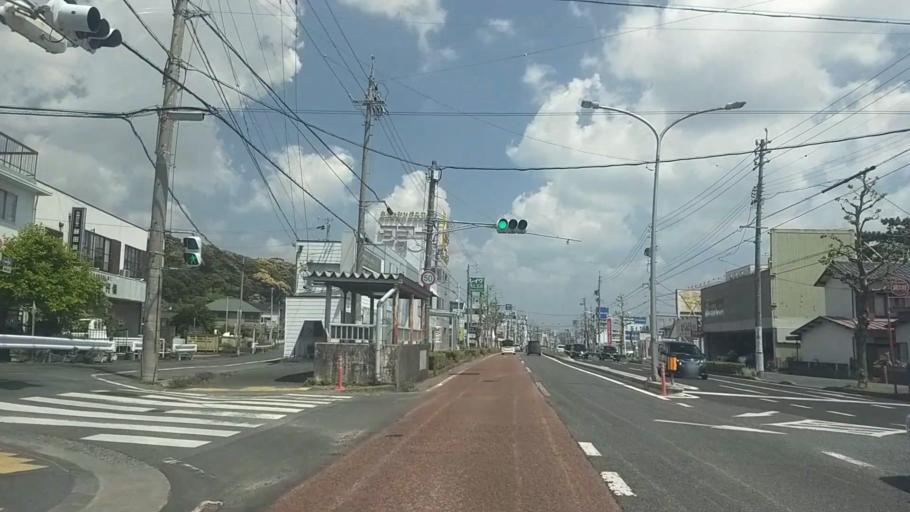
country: JP
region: Shizuoka
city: Hamamatsu
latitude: 34.7251
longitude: 137.7311
